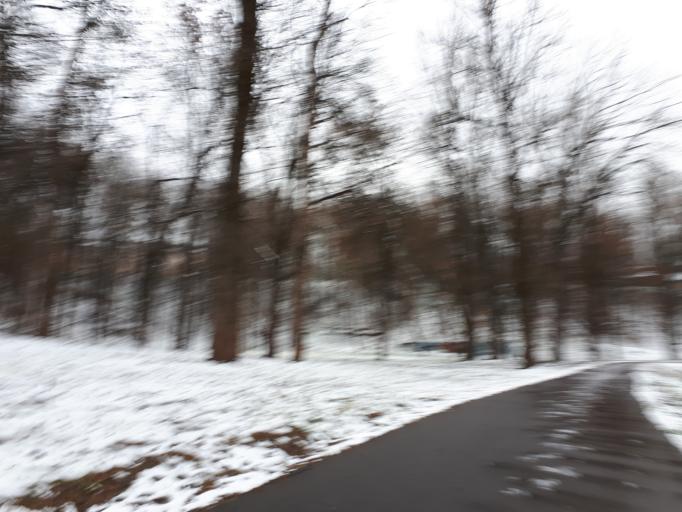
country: BY
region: Vitebsk
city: Vitebsk
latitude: 55.1987
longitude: 30.2113
